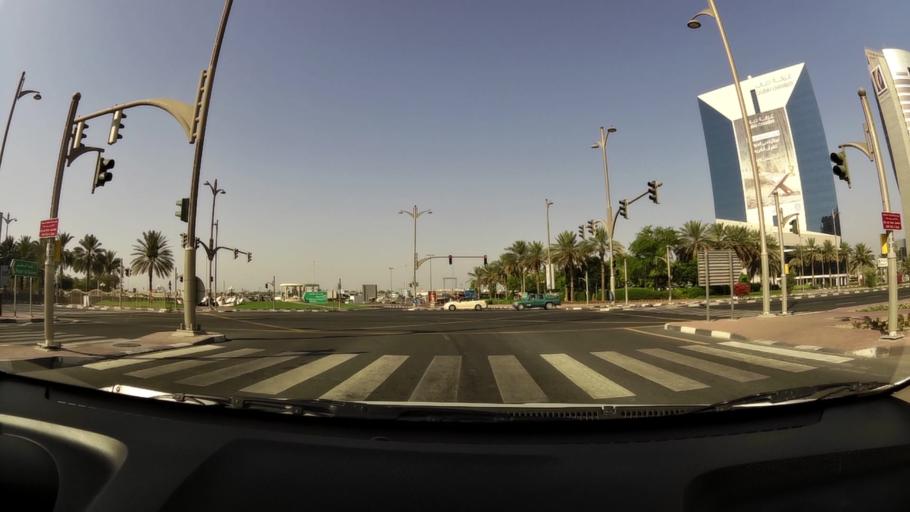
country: AE
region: Ash Shariqah
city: Sharjah
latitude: 25.2603
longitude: 55.3170
